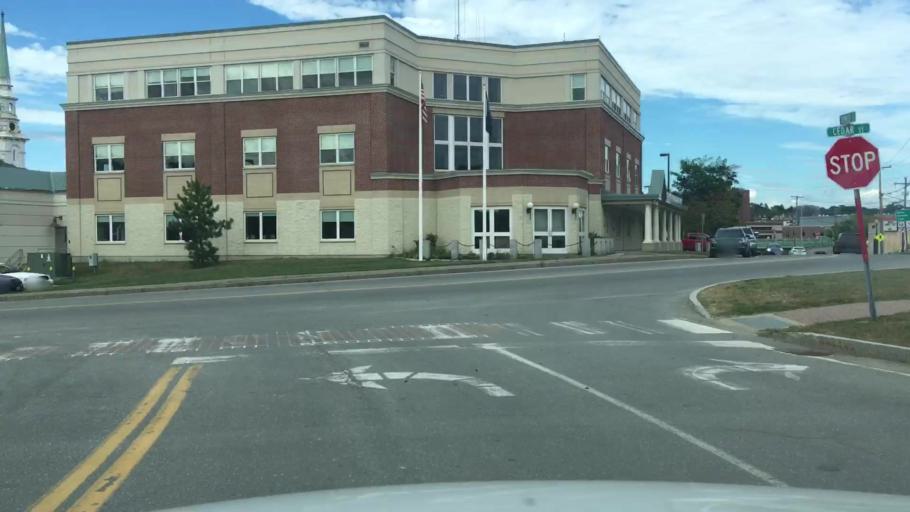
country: US
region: Maine
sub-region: Penobscot County
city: Bangor
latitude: 44.7965
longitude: -68.7724
